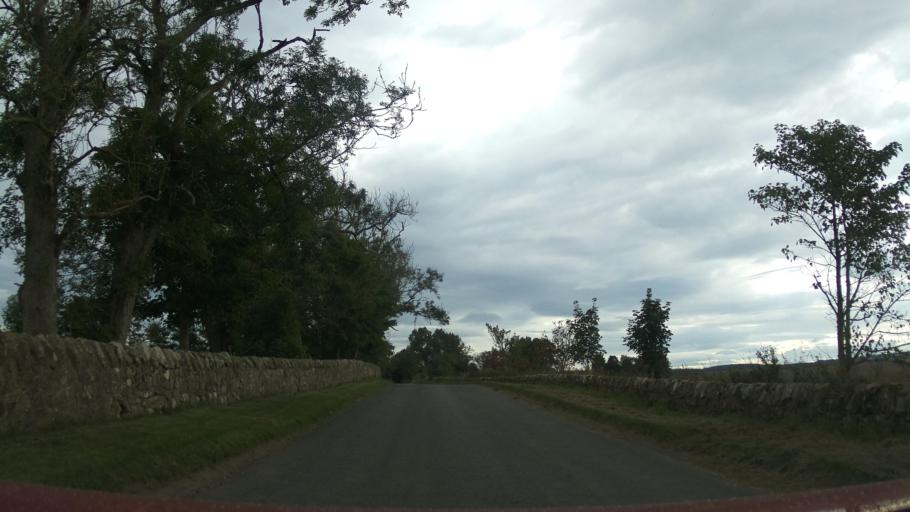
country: GB
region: Scotland
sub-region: Fife
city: Saint Andrews
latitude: 56.3173
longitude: -2.7798
